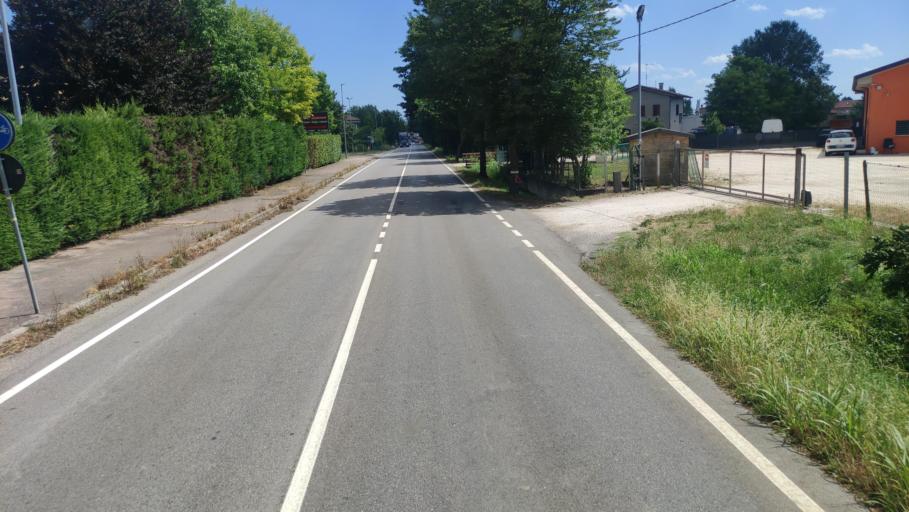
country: IT
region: Veneto
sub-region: Provincia di Venezia
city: Scorze
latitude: 45.5729
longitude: 12.0988
